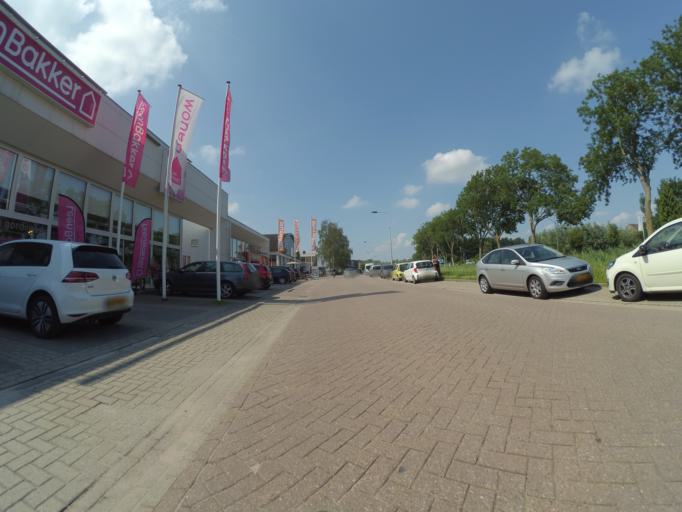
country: NL
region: Gelderland
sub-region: Gemeente Culemborg
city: Culemborg
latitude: 51.9454
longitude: 5.2191
